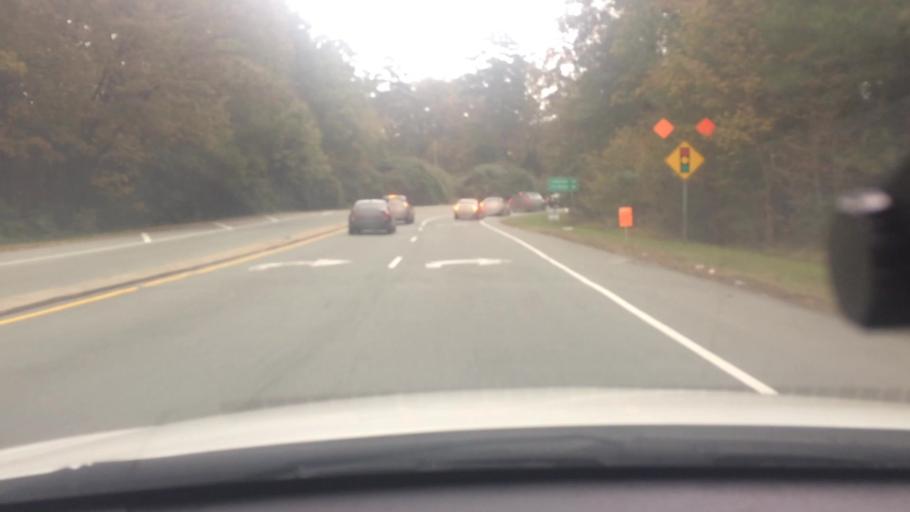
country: US
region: North Carolina
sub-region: Orange County
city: Chapel Hill
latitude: 35.9094
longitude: -79.0278
